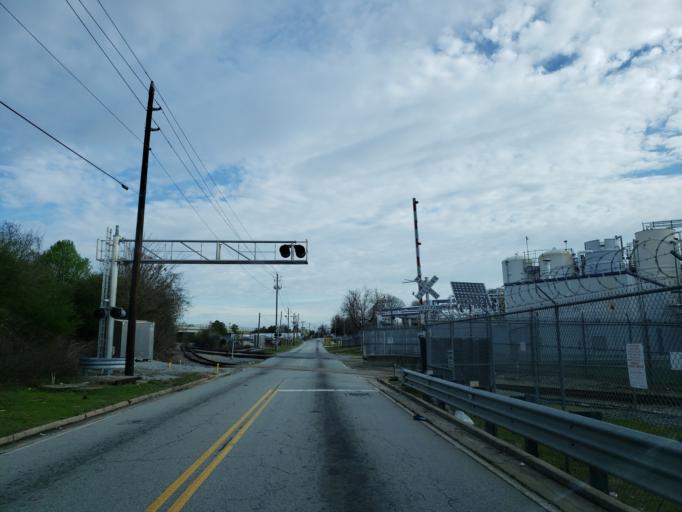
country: US
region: Georgia
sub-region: Clayton County
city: Forest Park
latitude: 33.6293
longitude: -84.3870
